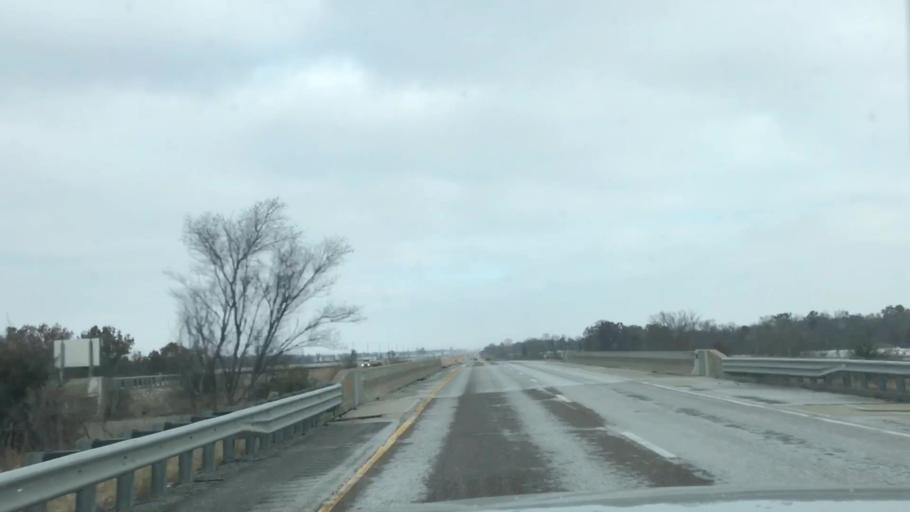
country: US
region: Illinois
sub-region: Macoupin County
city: Staunton
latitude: 38.9786
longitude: -89.7492
